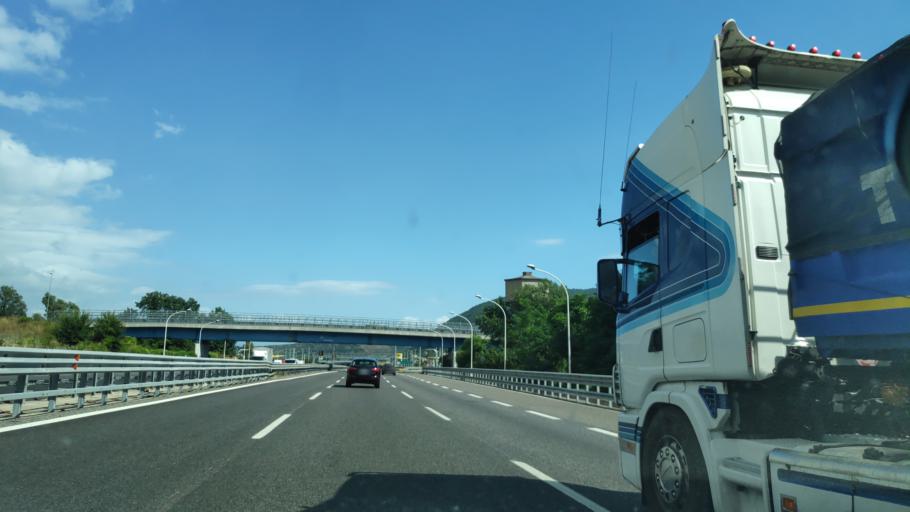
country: IT
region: Campania
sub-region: Provincia di Salerno
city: San Mango Piemonte
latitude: 40.6946
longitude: 14.8319
